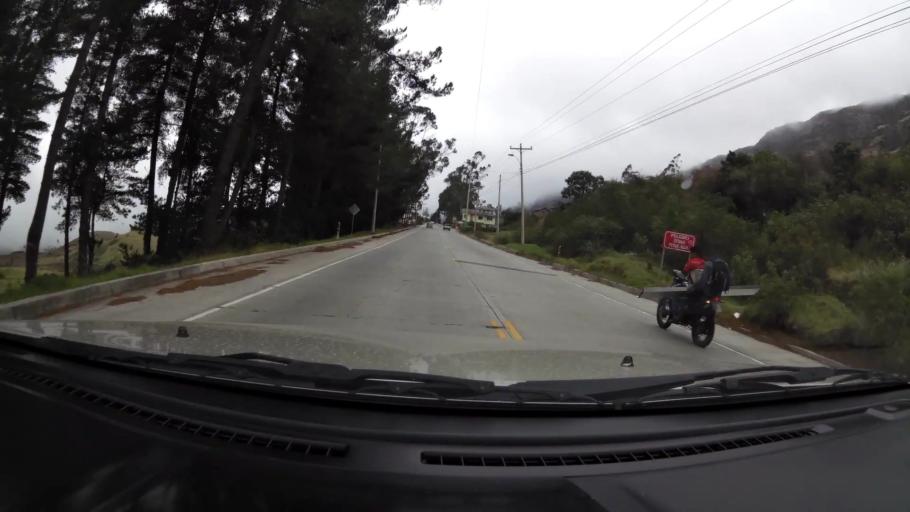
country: EC
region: Canar
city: Canar
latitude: -2.4796
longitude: -78.9797
